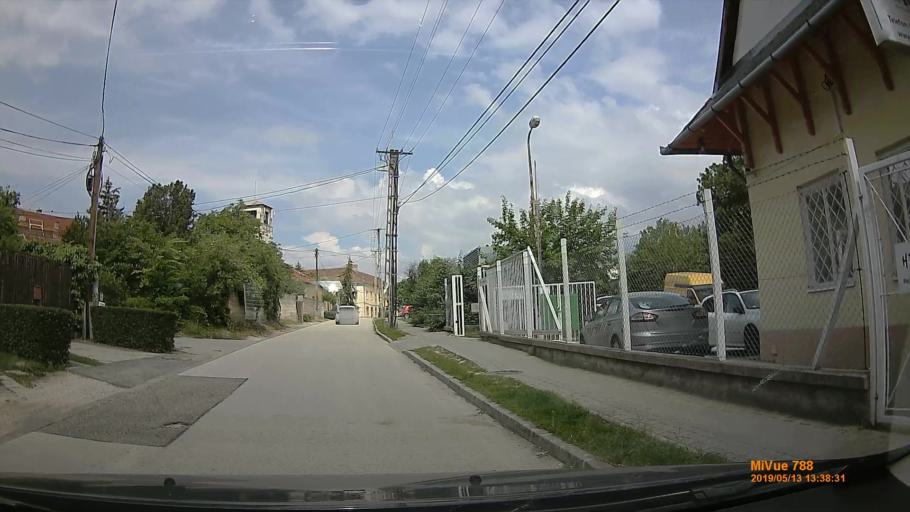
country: HU
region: Budapest
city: Budapest XXII. keruelet
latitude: 47.4127
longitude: 19.0164
